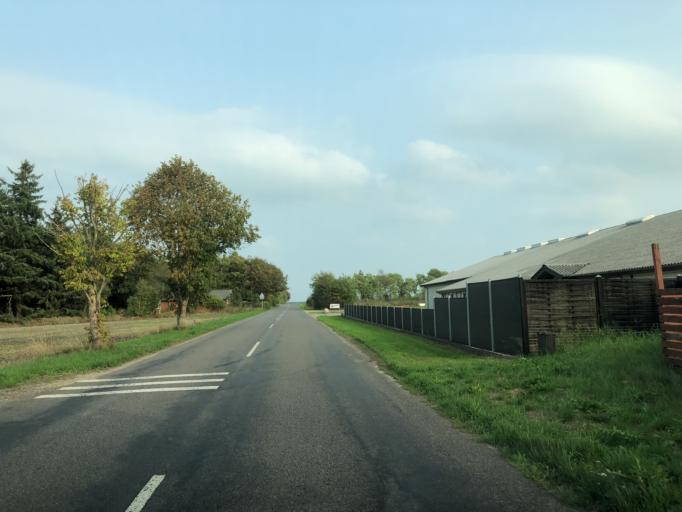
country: DK
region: Central Jutland
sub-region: Ringkobing-Skjern Kommune
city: Videbaek
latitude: 56.0538
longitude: 8.6925
